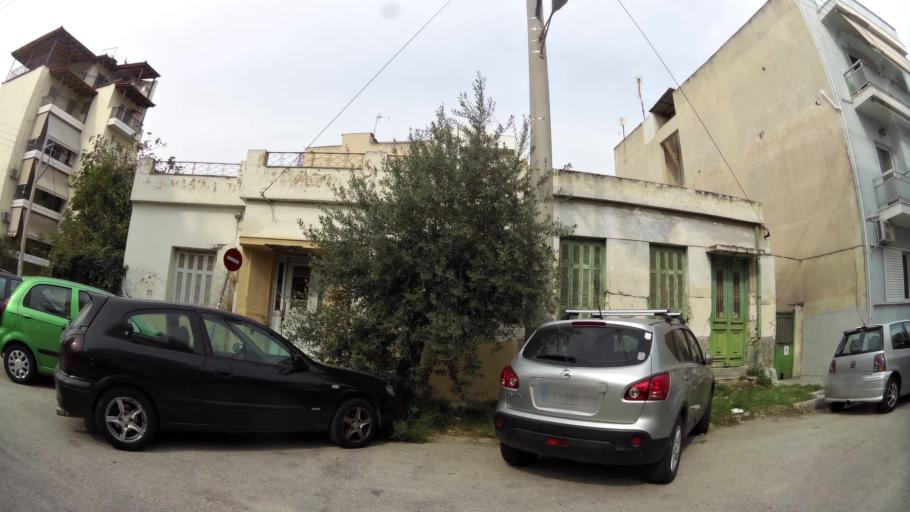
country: GR
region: Attica
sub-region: Nomos Piraios
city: Agios Ioannis Rentis
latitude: 37.9510
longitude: 23.6588
